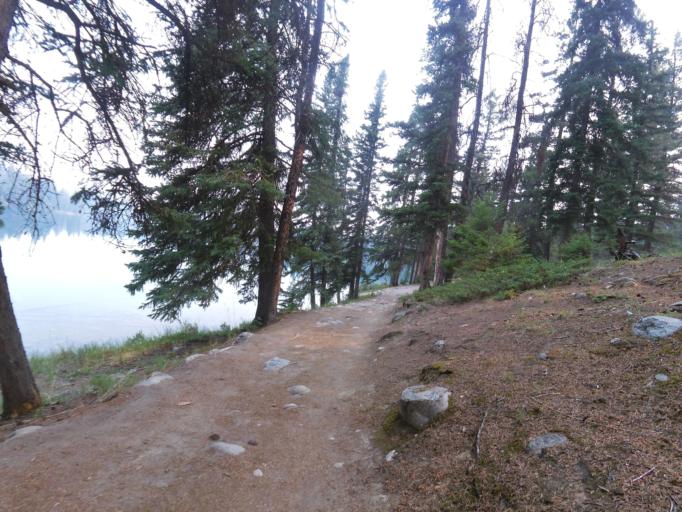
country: CA
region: Alberta
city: Jasper Park Lodge
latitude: 52.8815
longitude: -118.0540
